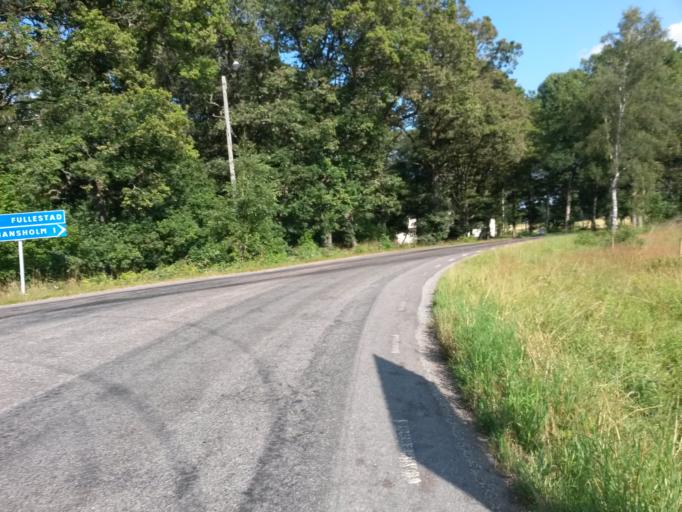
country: SE
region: Vaestra Goetaland
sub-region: Vargarda Kommun
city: Jonstorp
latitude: 58.0135
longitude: 12.7009
